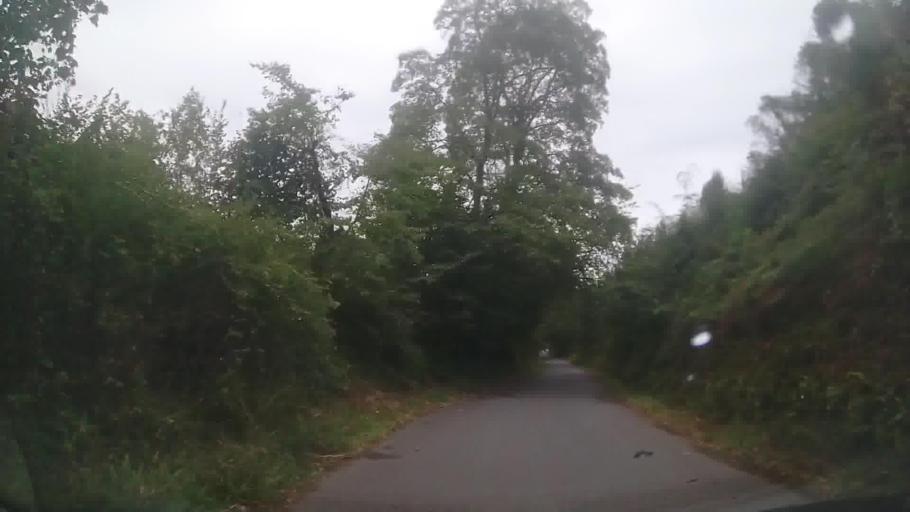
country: GB
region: Wales
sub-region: Pembrokeshire
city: Saundersfoot
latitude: 51.7376
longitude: -4.6594
